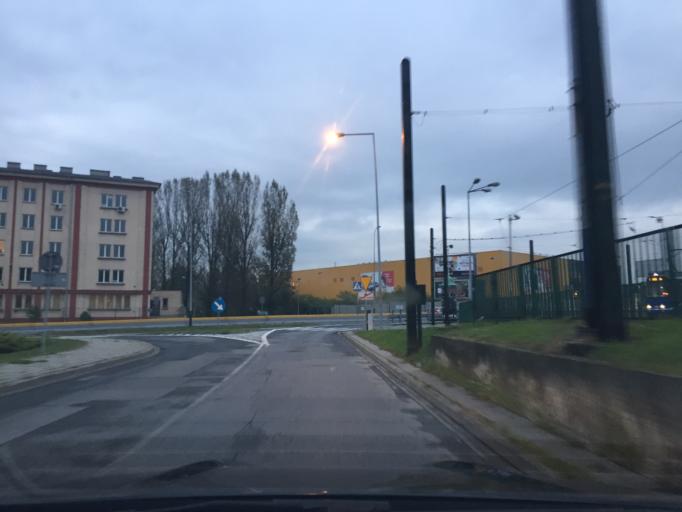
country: PL
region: Lesser Poland Voivodeship
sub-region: Krakow
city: Krakow
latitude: 50.0131
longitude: 19.9273
